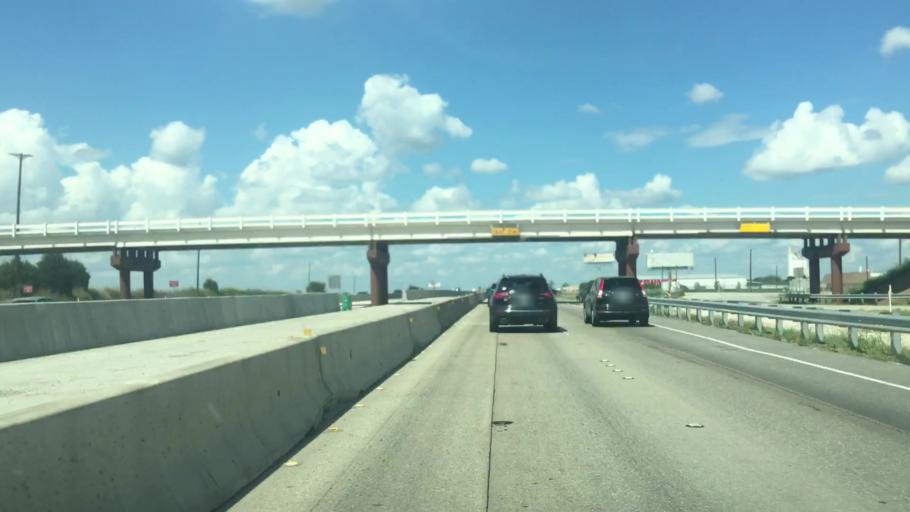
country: US
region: Texas
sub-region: Ellis County
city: Oak Leaf
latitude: 32.4740
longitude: -96.8363
